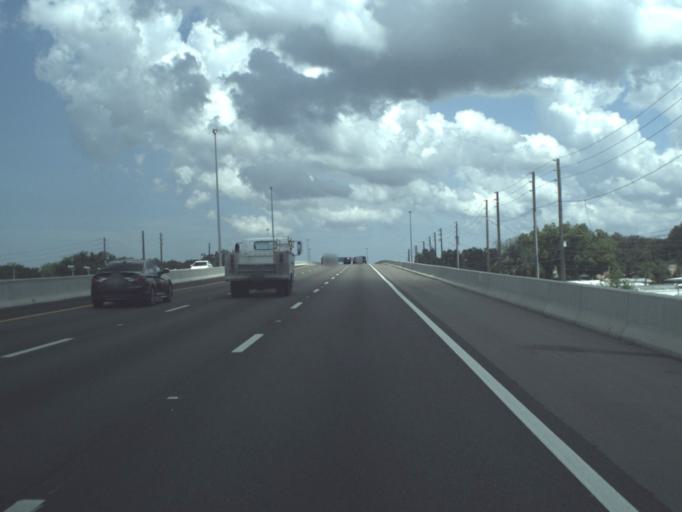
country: US
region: Florida
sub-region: Pinellas County
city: South Highpoint
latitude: 27.9514
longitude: -82.7300
